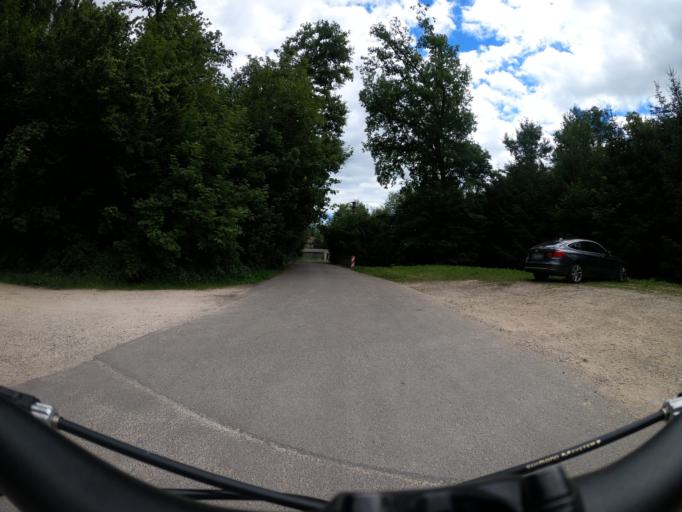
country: DE
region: Bavaria
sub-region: Swabia
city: Nersingen
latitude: 48.4353
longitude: 10.1074
